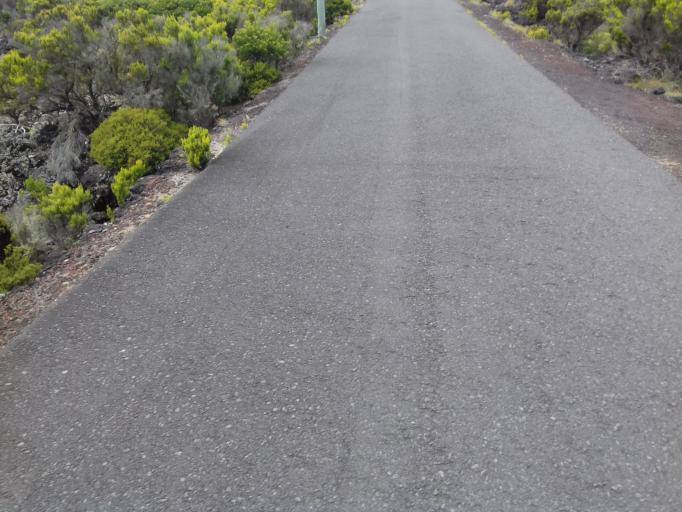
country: PT
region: Azores
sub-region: Sao Roque do Pico
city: Sao Roque do Pico
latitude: 38.4121
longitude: -28.0327
